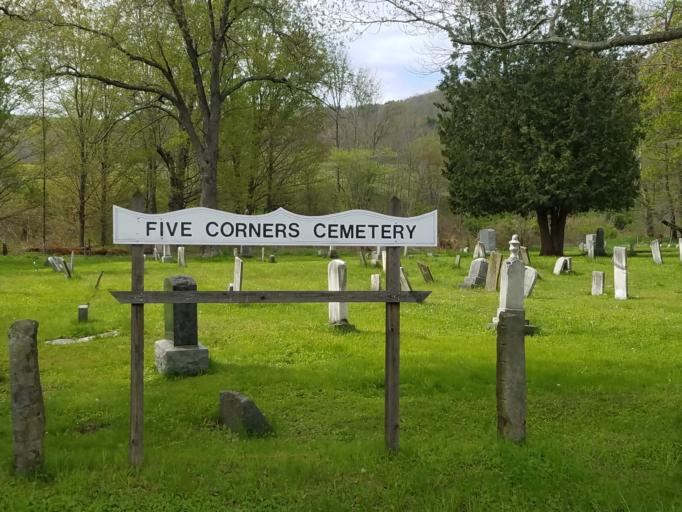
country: US
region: New York
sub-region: Steuben County
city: Canisteo
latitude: 42.1128
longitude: -77.4934
